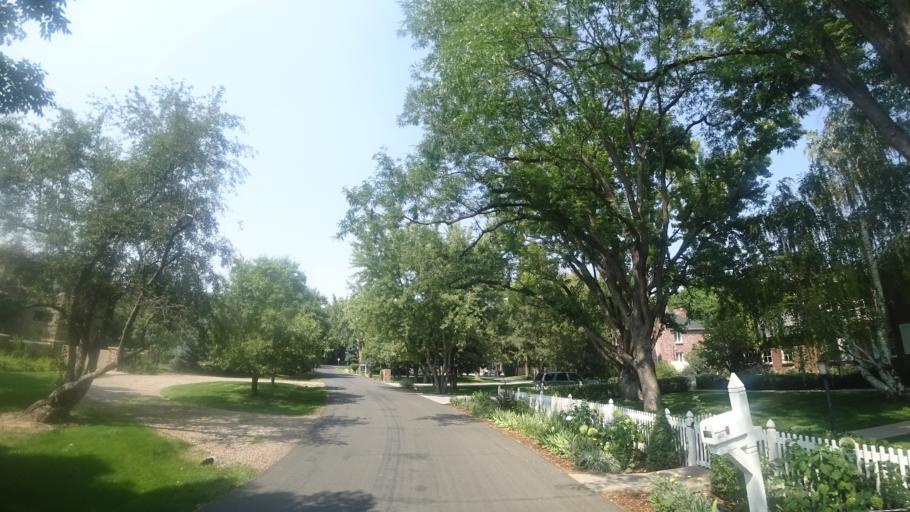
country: US
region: Colorado
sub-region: Arapahoe County
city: Cherry Hills Village
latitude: 39.6284
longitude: -104.9713
